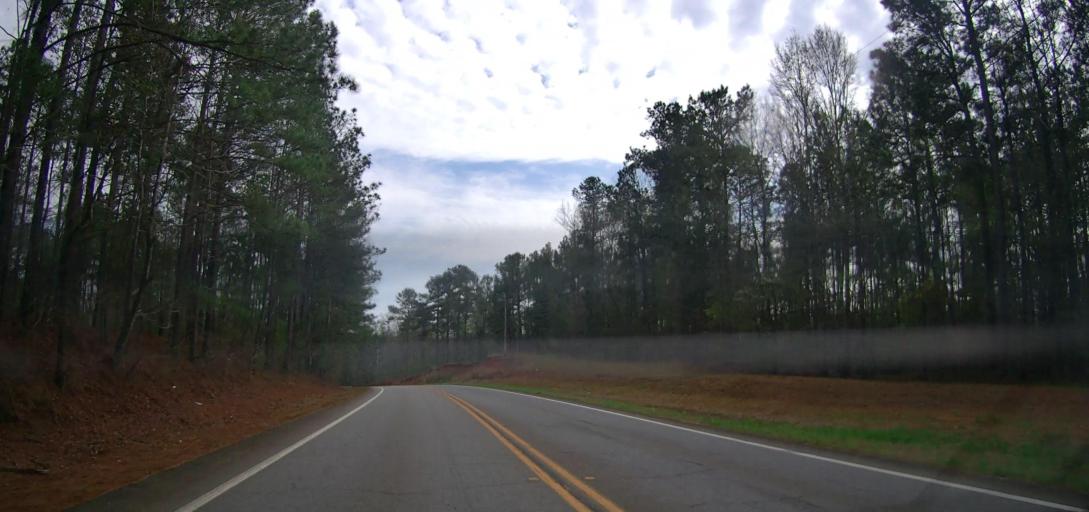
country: US
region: Georgia
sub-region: Jones County
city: Gray
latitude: 32.9904
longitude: -83.6850
